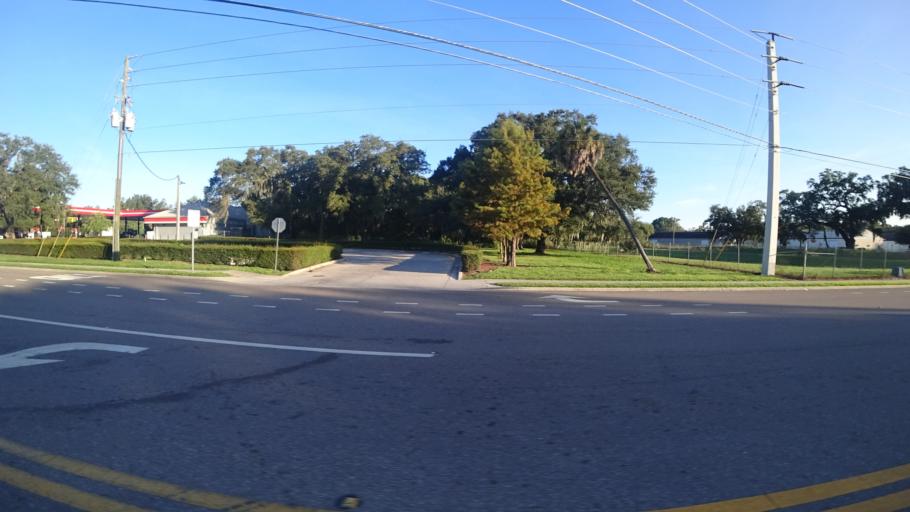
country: US
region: Florida
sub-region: Manatee County
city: Memphis
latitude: 27.5284
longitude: -82.5593
